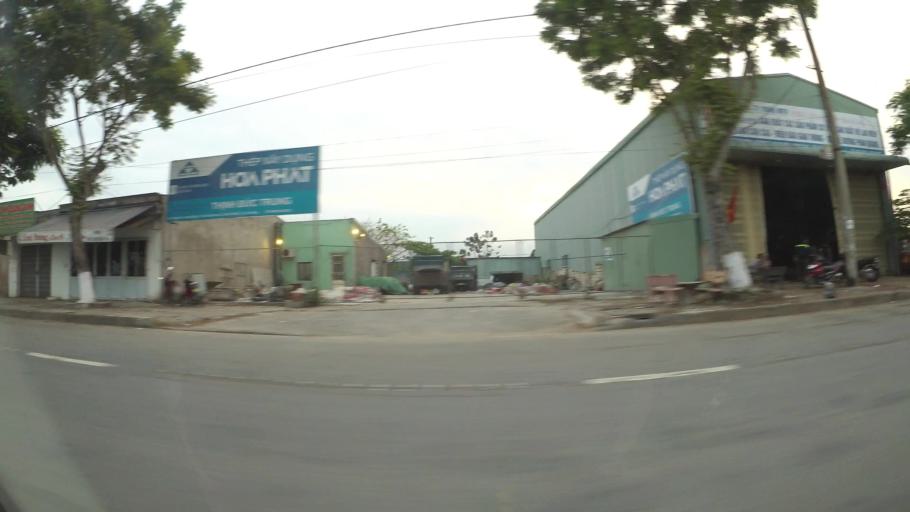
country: VN
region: Da Nang
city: Lien Chieu
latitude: 16.0945
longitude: 108.1387
